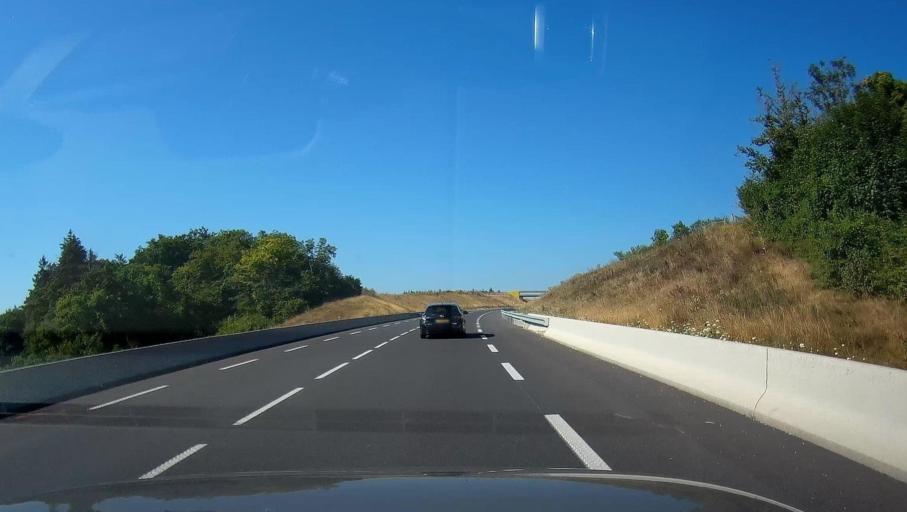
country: FR
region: Lorraine
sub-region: Departement de Meurthe-et-Moselle
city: Colombey-les-Belles
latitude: 48.5492
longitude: 5.9166
